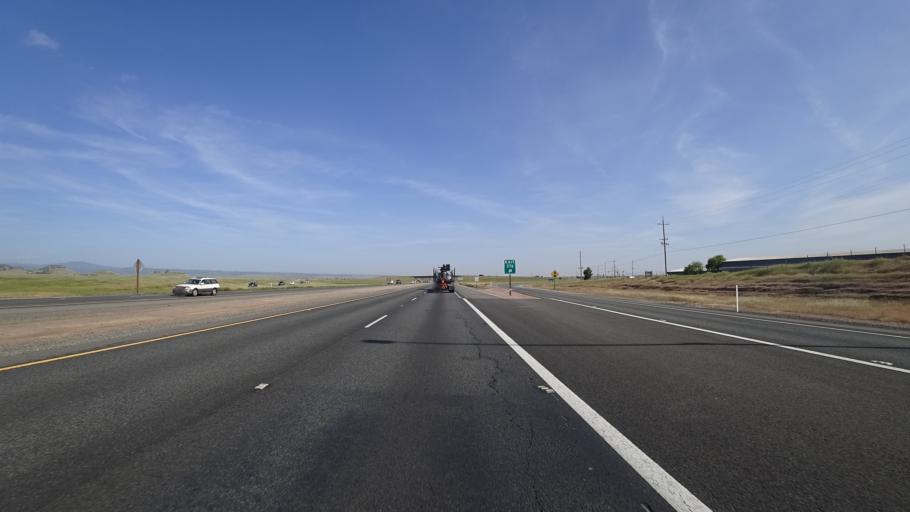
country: US
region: California
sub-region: Butte County
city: Durham
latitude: 39.6455
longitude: -121.7199
